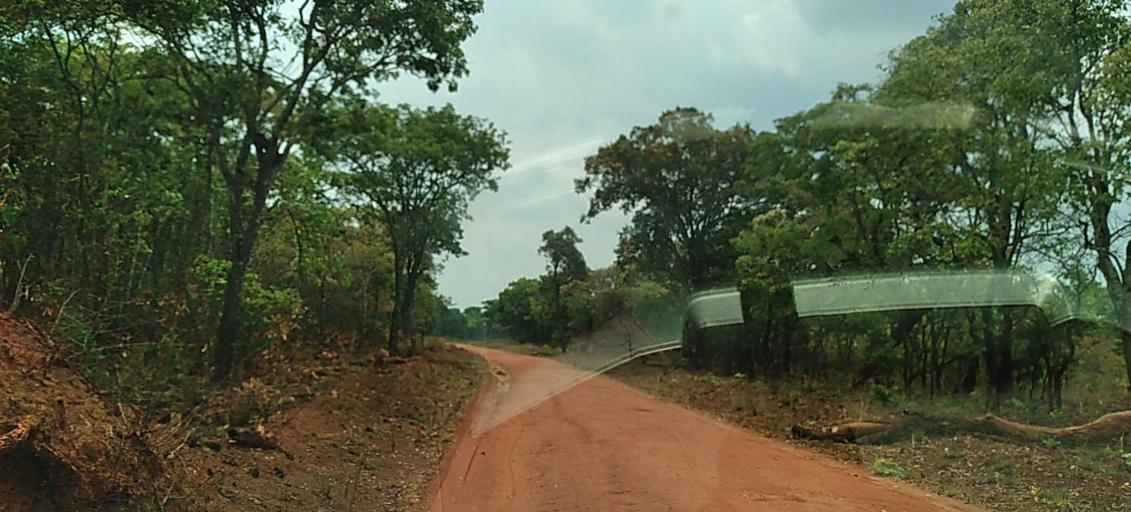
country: ZM
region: North-Western
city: Mwinilunga
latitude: -11.5551
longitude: 24.7732
